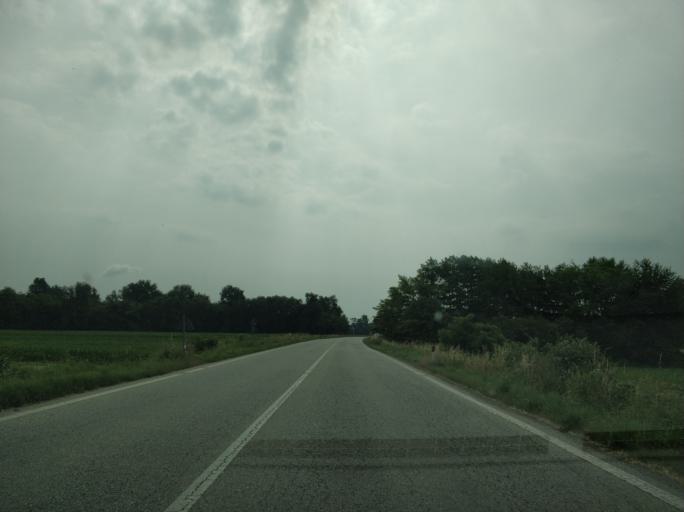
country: IT
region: Piedmont
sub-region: Provincia di Torino
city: Montalenghe
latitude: 45.3148
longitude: 7.8325
